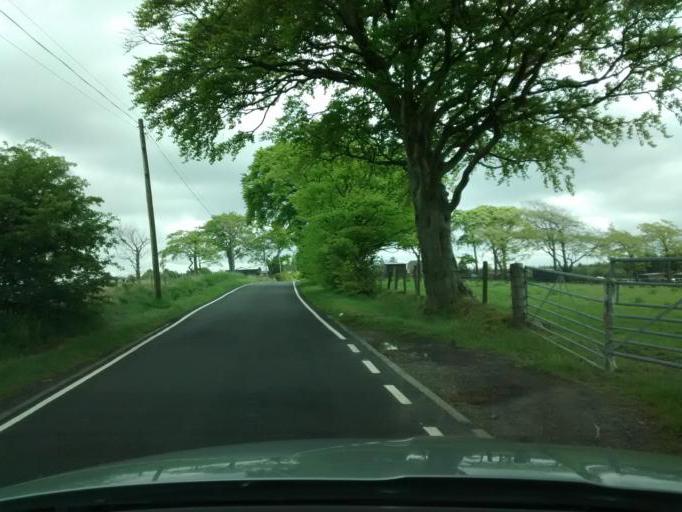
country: GB
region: Scotland
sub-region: North Lanarkshire
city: Harthill
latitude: 55.8804
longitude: -3.7414
